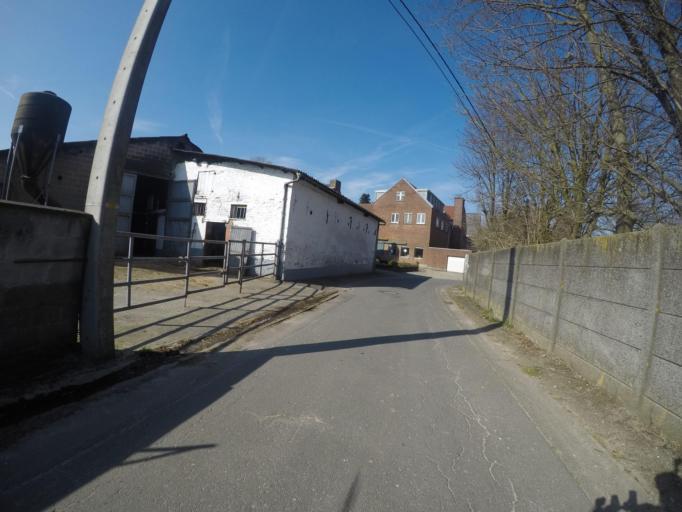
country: BE
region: Flanders
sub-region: Provincie Oost-Vlaanderen
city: Sint-Maria-Lierde
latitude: 50.7851
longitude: 3.8407
